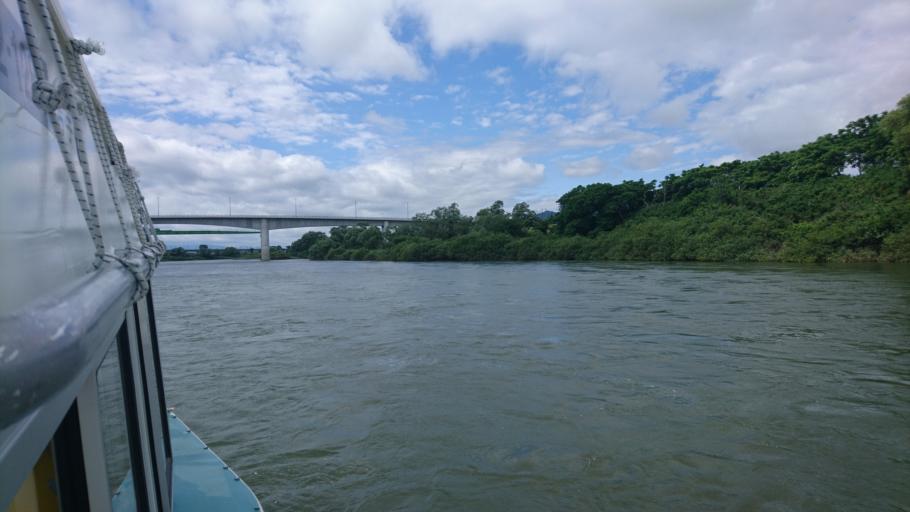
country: JP
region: Iwate
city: Ichinoseki
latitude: 38.9526
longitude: 141.1619
